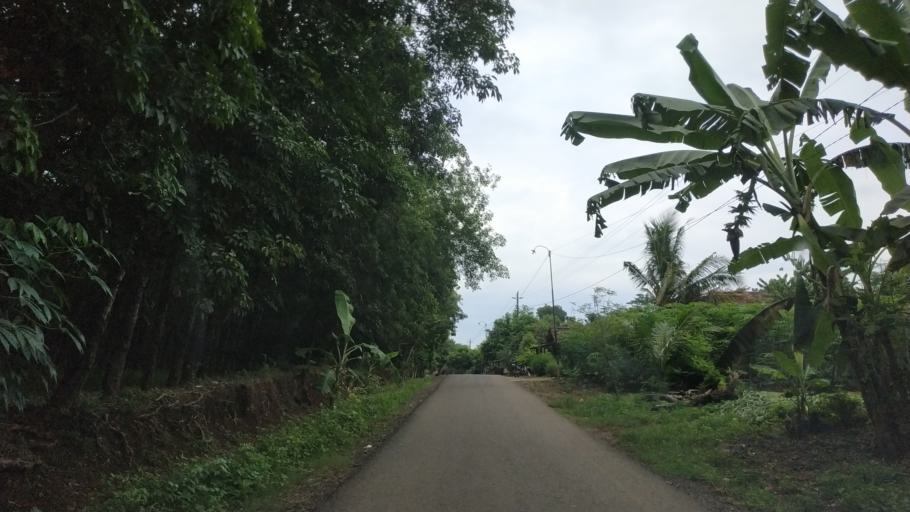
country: ID
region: Central Java
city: Krajan Tegalombo
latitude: -6.4357
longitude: 110.9820
